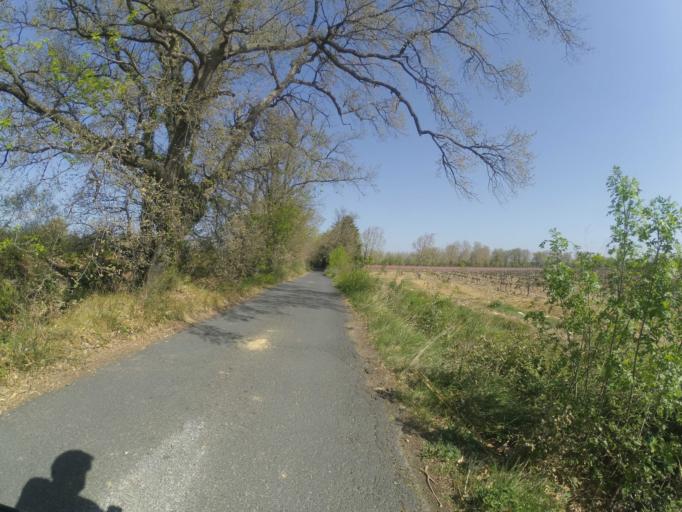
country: FR
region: Languedoc-Roussillon
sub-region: Departement des Pyrenees-Orientales
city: Thuir
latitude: 42.6614
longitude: 2.7591
